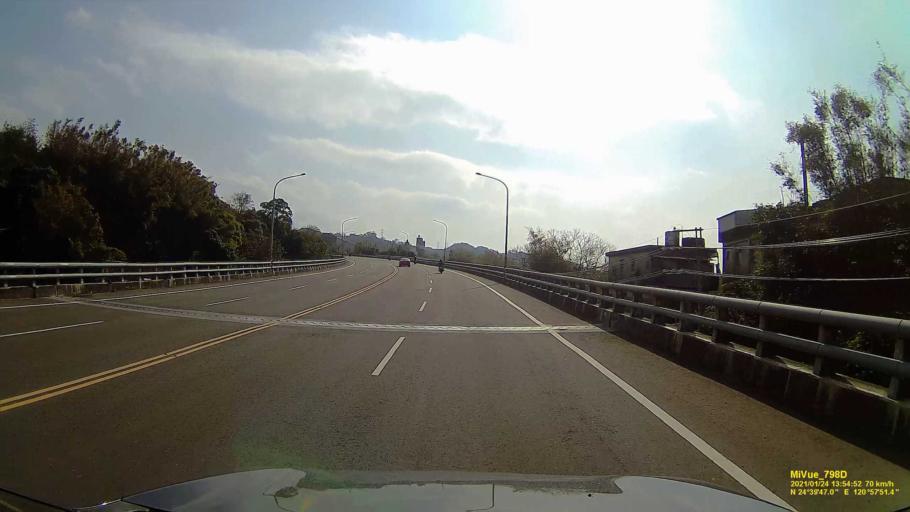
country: TW
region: Taiwan
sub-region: Hsinchu
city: Hsinchu
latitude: 24.6627
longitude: 120.9641
